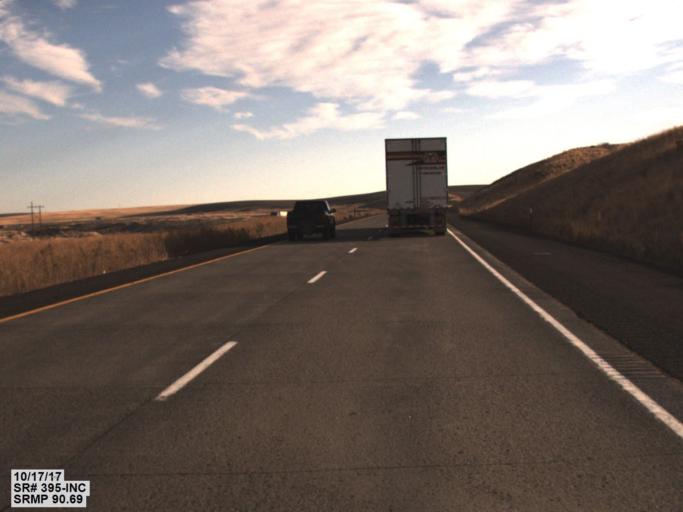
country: US
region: Washington
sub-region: Adams County
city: Ritzville
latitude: 47.0491
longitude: -118.4357
